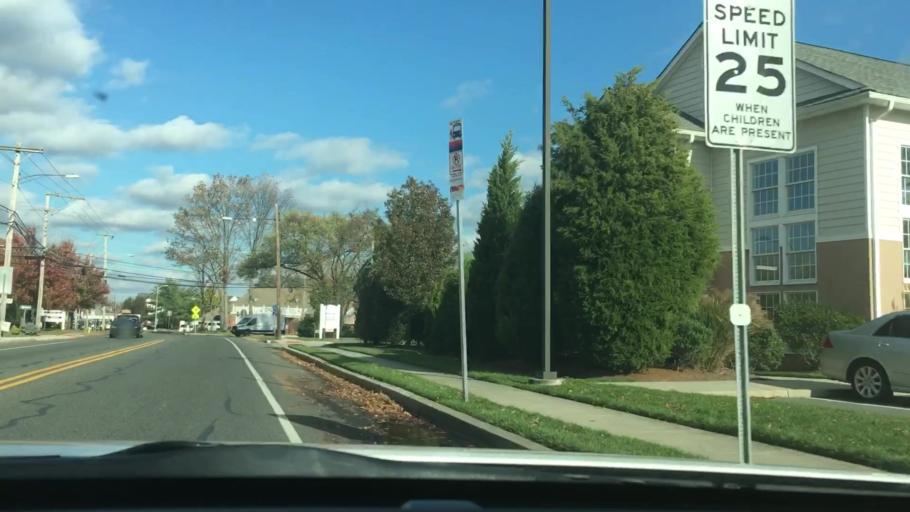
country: US
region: New Jersey
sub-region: Atlantic County
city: Northfield
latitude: 39.3693
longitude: -74.5595
